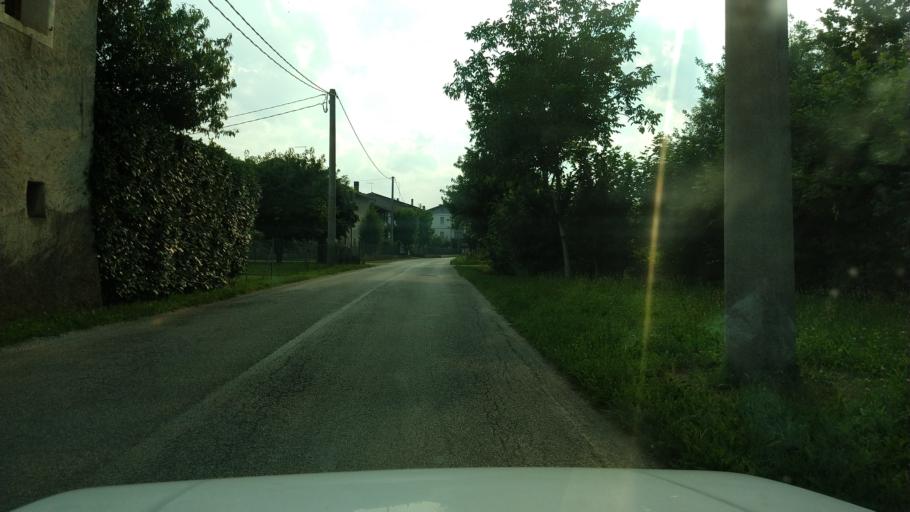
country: IT
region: Veneto
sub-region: Provincia di Vicenza
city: Schiavon
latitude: 45.7119
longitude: 11.6435
